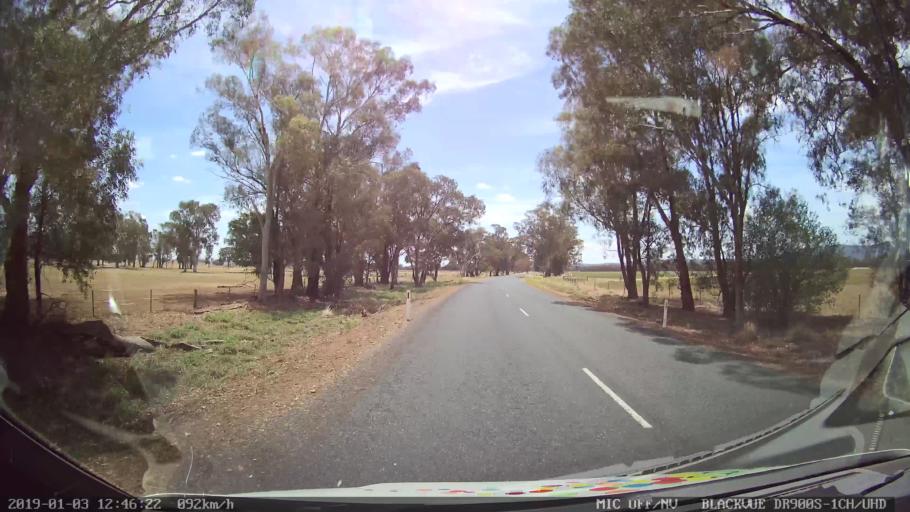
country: AU
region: New South Wales
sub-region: Weddin
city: Grenfell
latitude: -33.7389
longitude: 148.2325
